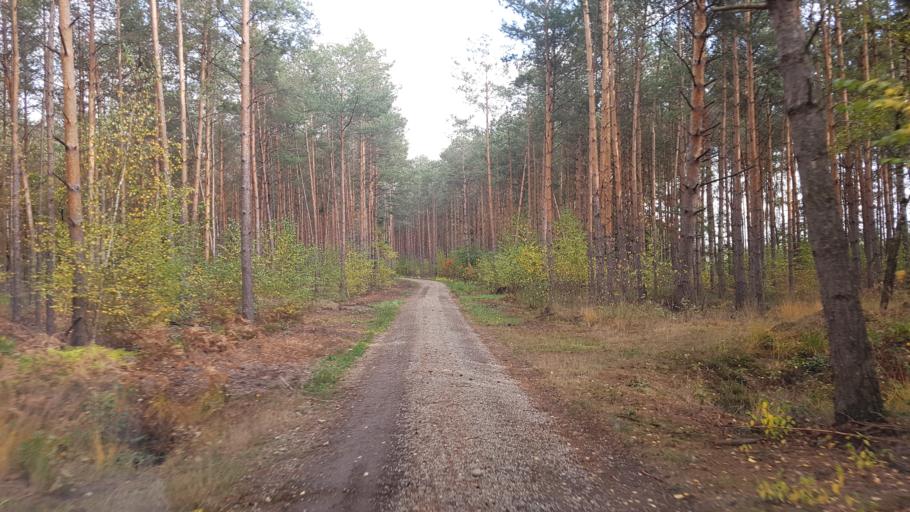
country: DE
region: Brandenburg
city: Schonborn
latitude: 51.6226
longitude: 13.5186
